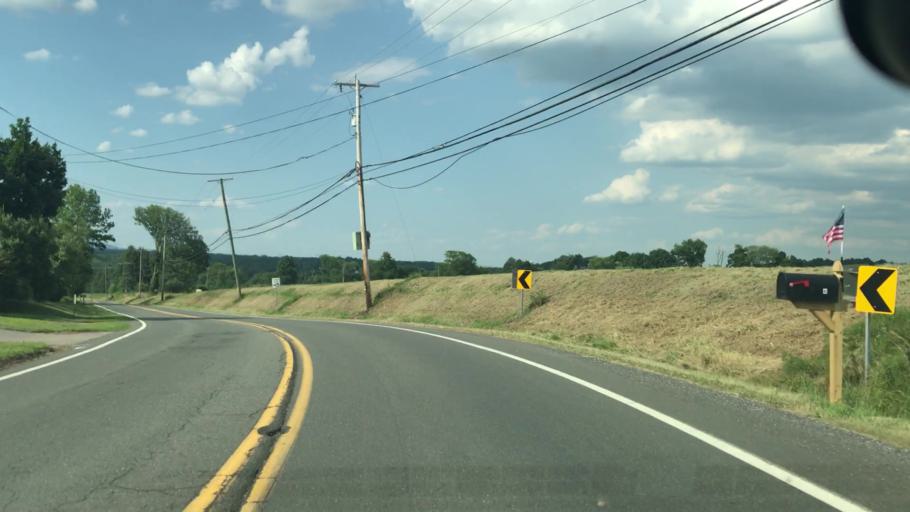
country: US
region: New Jersey
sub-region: Hunterdon County
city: Flemington
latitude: 40.4604
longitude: -74.8299
